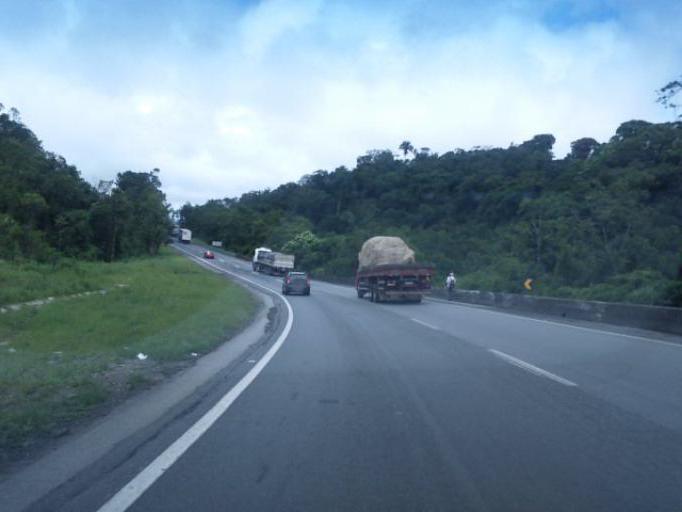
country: BR
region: Parana
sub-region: Antonina
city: Antonina
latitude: -25.1052
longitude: -48.7157
